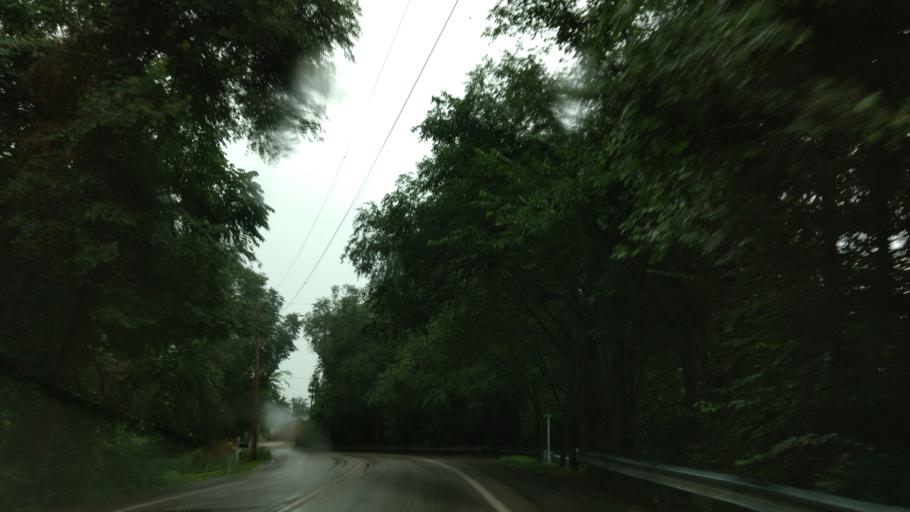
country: US
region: Pennsylvania
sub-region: Allegheny County
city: McKees Rocks
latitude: 40.4808
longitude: -80.0828
